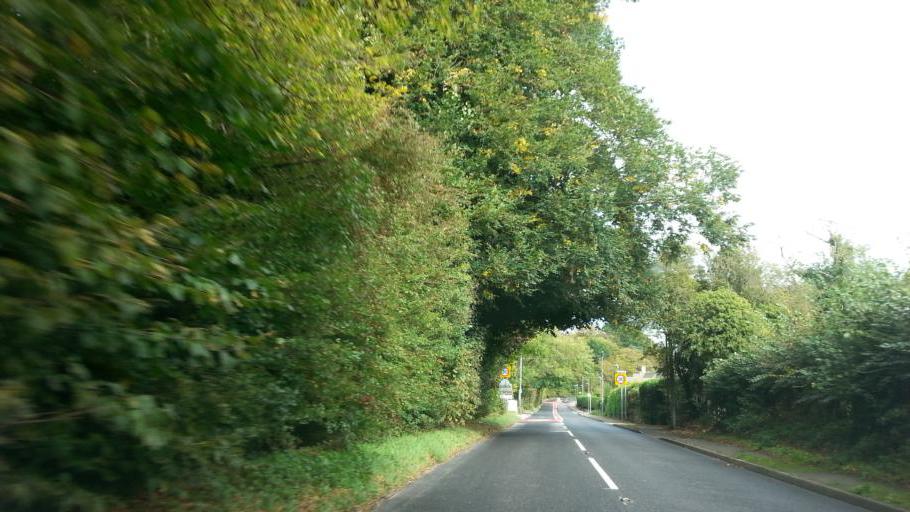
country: GB
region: England
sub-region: Gloucestershire
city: Painswick
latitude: 51.7813
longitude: -2.2031
